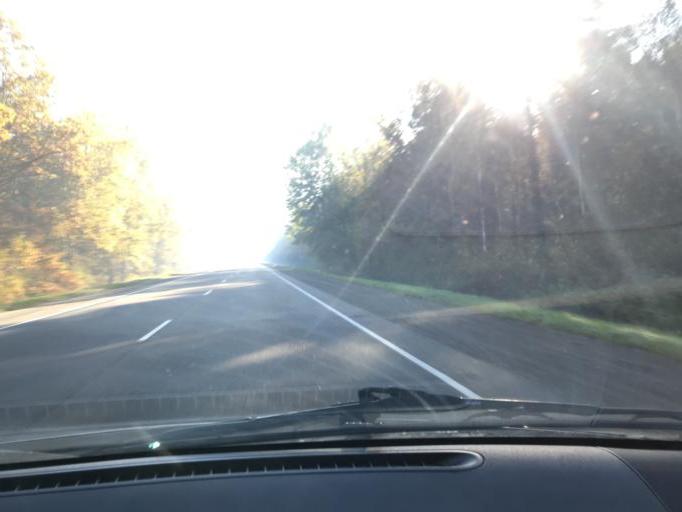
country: BY
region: Brest
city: Horad Luninyets
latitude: 52.2912
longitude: 26.7714
